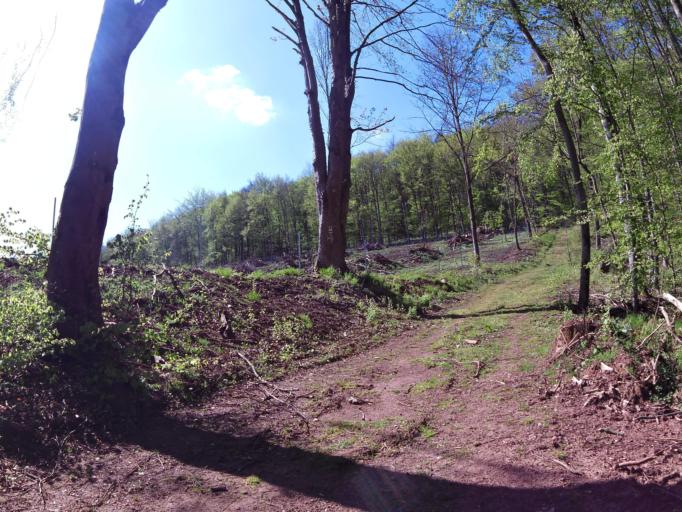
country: DE
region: Thuringia
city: Eisenach
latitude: 50.9685
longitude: 10.2926
